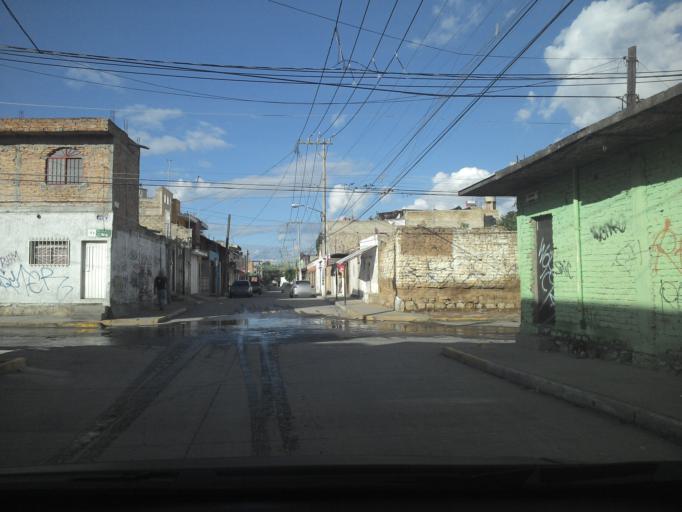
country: MX
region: Jalisco
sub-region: Tlajomulco de Zuniga
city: Palomar
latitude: 20.6208
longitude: -103.4542
